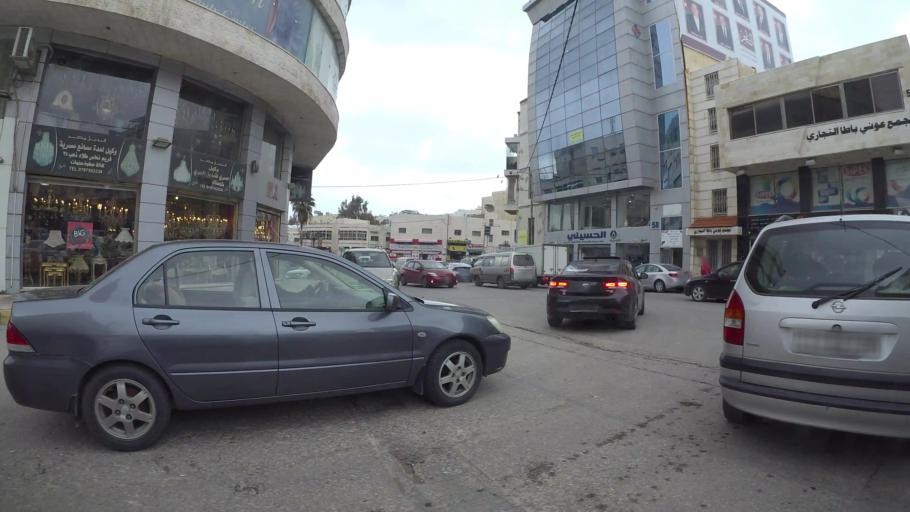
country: JO
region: Amman
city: Al Jubayhah
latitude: 31.9894
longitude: 35.8490
